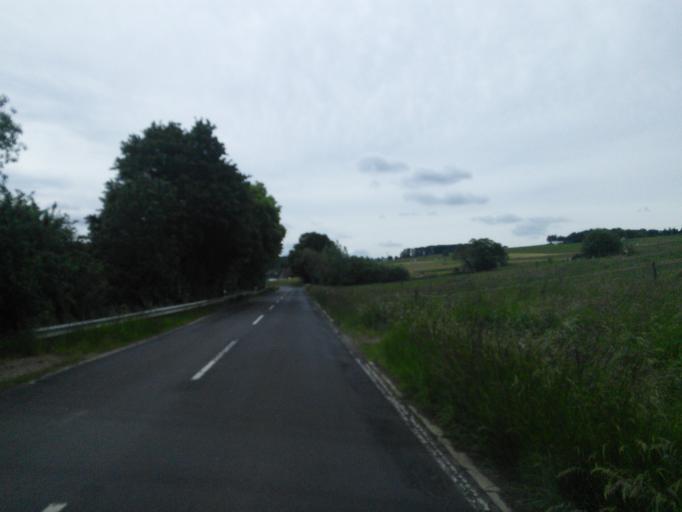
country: DE
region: North Rhine-Westphalia
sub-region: Regierungsbezirk Koln
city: Rheinbach
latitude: 50.5933
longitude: 6.8974
